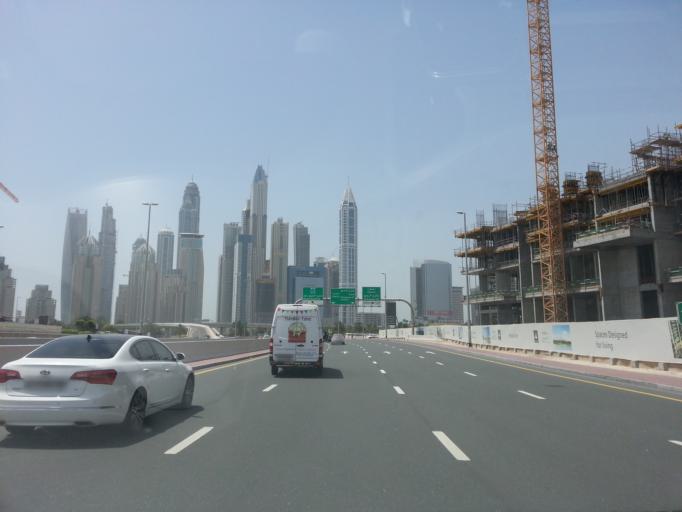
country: AE
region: Dubai
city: Dubai
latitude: 25.0791
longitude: 55.1569
